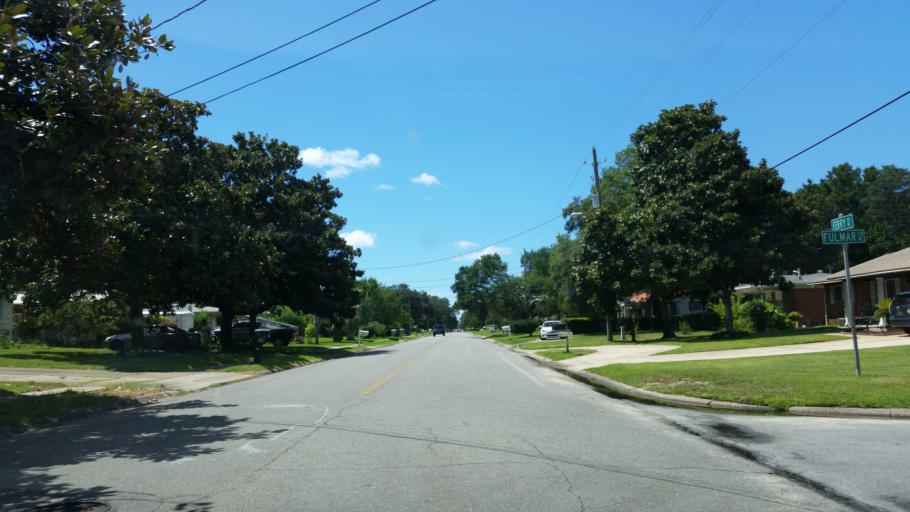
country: US
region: Florida
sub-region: Okaloosa County
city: Ocean City
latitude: 30.4227
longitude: -86.5936
